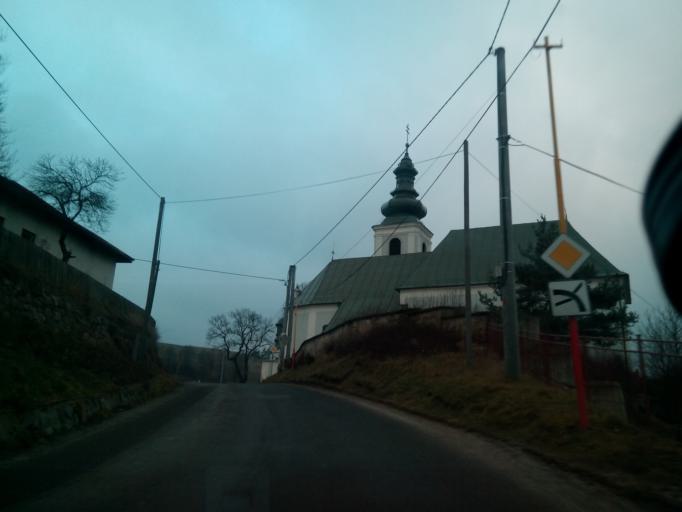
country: SK
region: Kosicky
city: Krompachy
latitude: 48.9221
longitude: 20.9373
